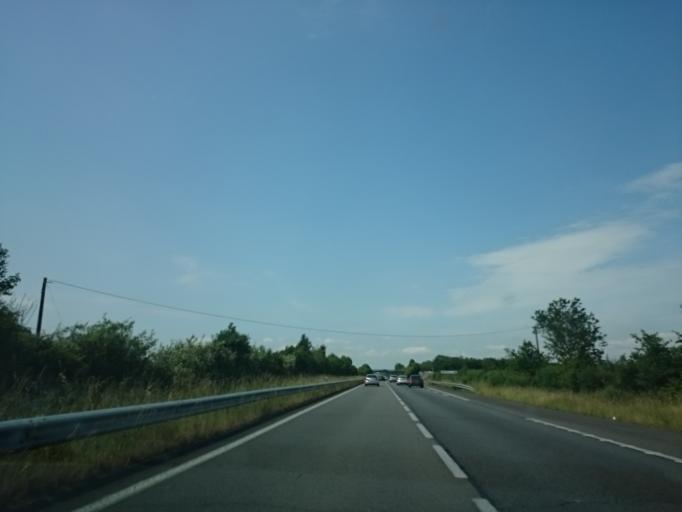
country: FR
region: Pays de la Loire
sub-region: Departement de la Loire-Atlantique
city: La Grigonnais
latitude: 47.4863
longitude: -1.6371
